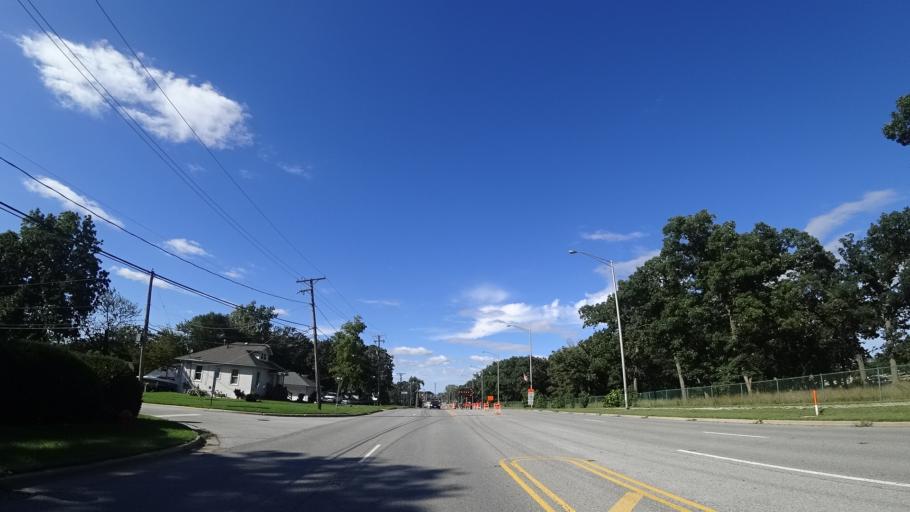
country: US
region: Illinois
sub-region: Cook County
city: Oak Forest
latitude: 41.5996
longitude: -87.7364
